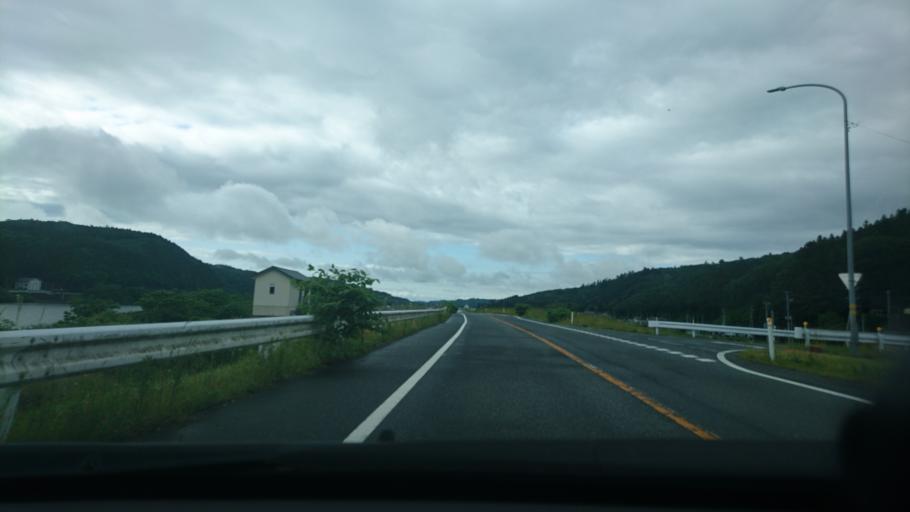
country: JP
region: Miyagi
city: Wakuya
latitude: 38.6240
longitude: 141.2955
